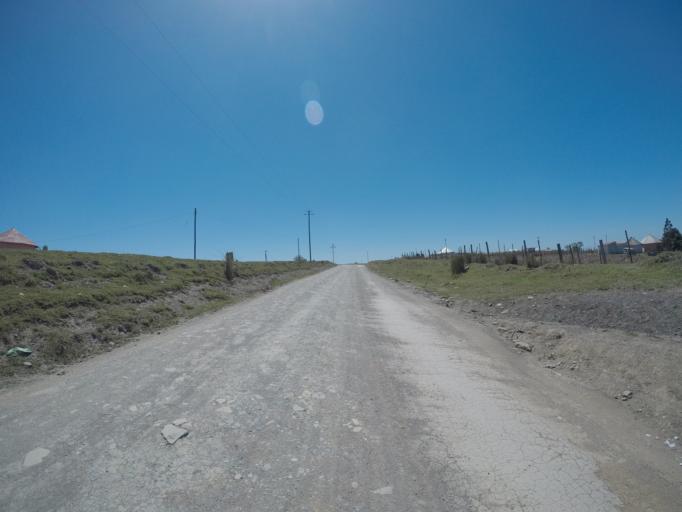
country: ZA
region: Eastern Cape
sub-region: OR Tambo District Municipality
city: Libode
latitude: -31.9465
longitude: 29.0255
